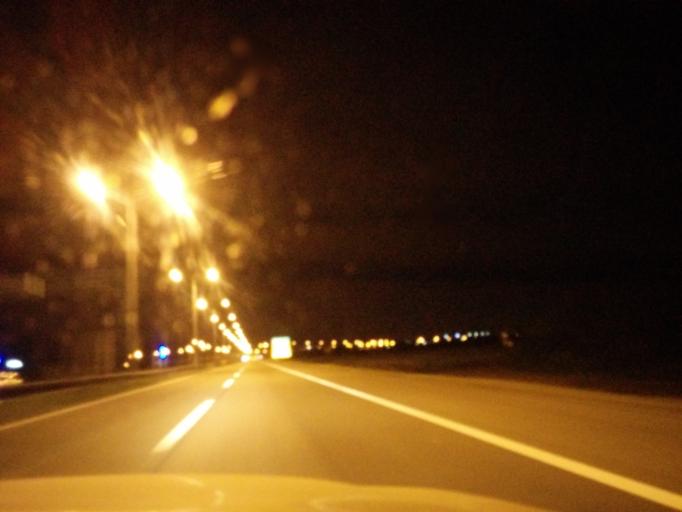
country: RS
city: Dobanovci
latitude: 44.8422
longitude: 20.2201
